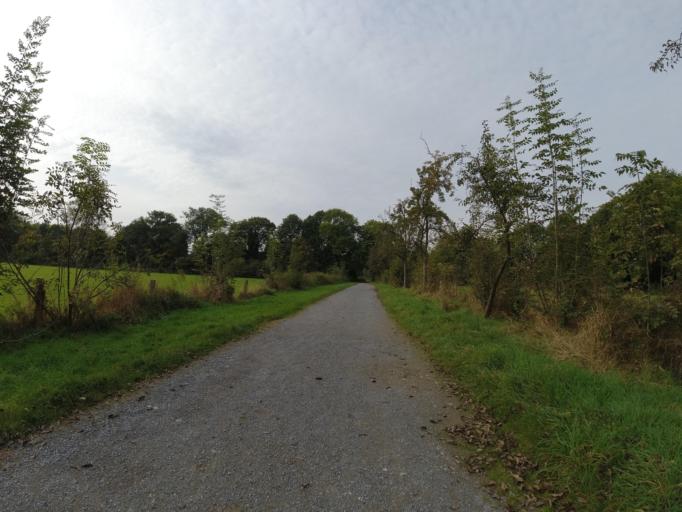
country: DE
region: North Rhine-Westphalia
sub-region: Regierungsbezirk Dusseldorf
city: Hochfeld
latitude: 51.3767
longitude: 6.6926
